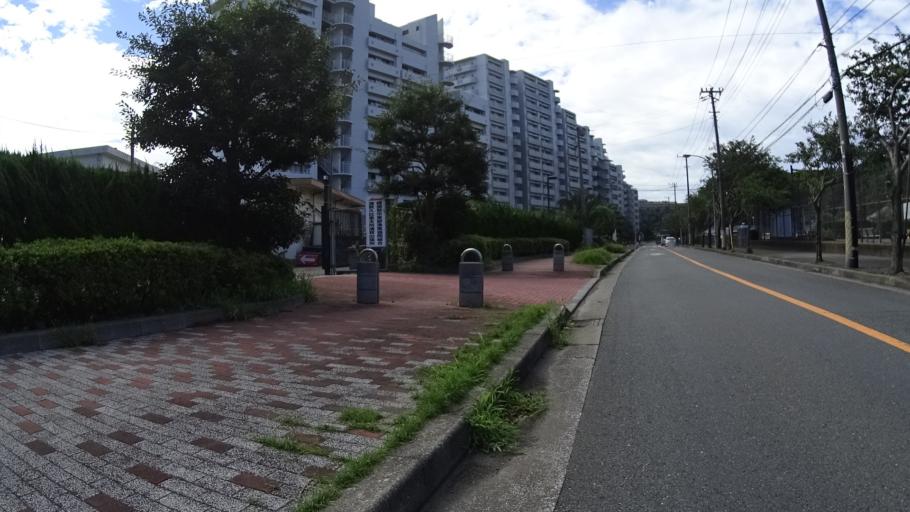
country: JP
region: Kanagawa
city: Yokosuka
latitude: 35.2379
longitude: 139.7218
